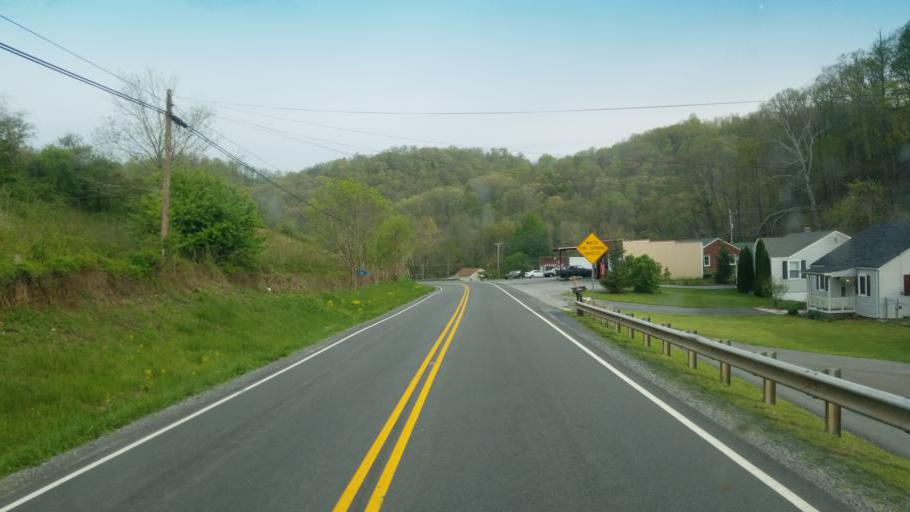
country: US
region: Virginia
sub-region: Smyth County
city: Marion
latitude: 36.8219
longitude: -81.4728
